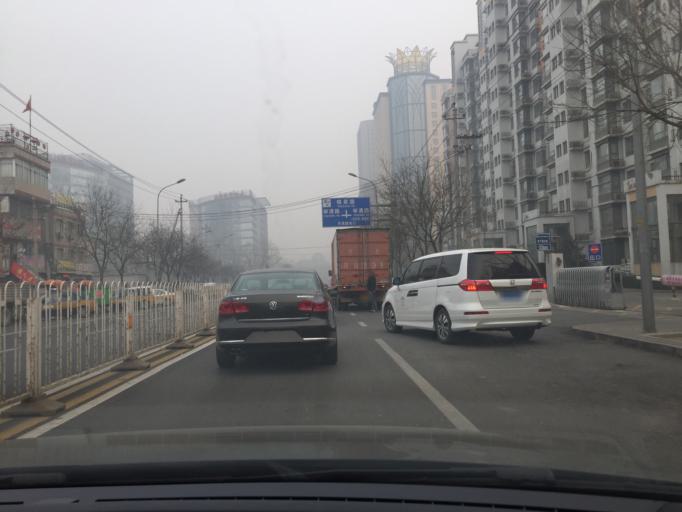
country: CN
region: Beijing
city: Qinghe
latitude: 40.0138
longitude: 116.3438
